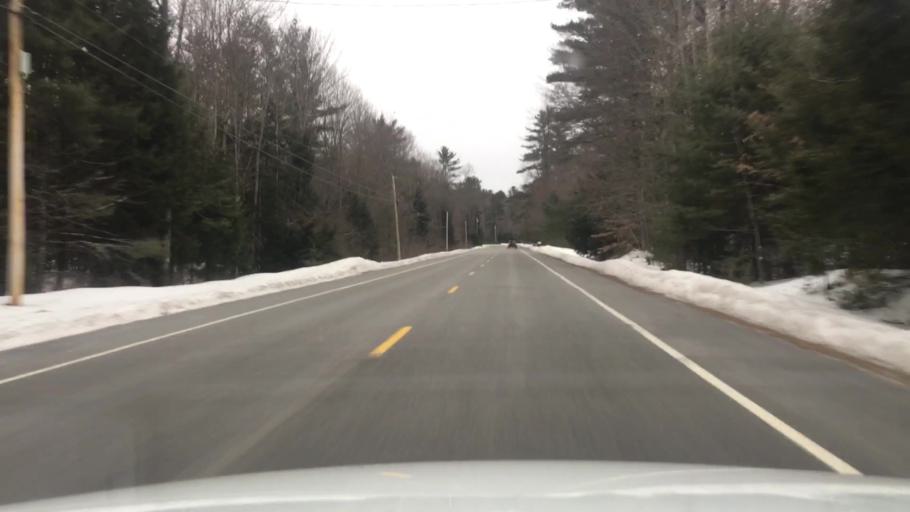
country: US
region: Maine
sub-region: York County
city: Limerick
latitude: 43.7217
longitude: -70.8137
